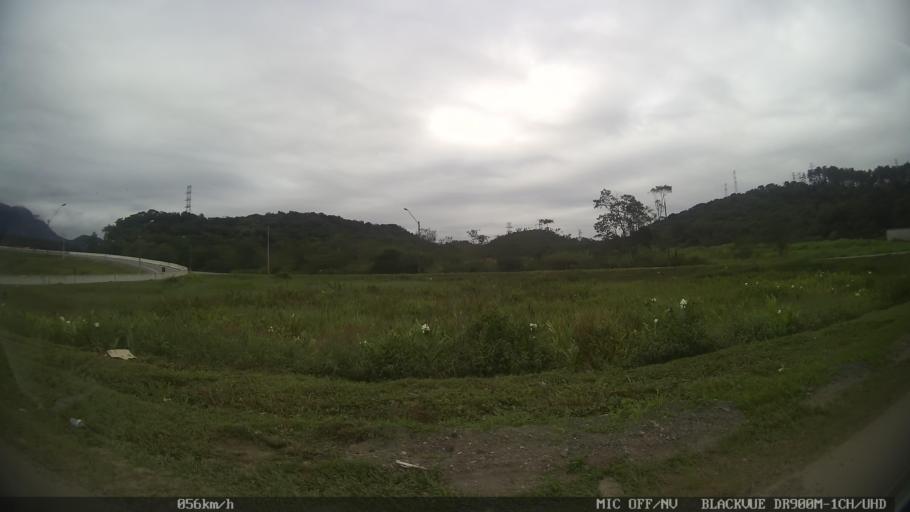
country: BR
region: Santa Catarina
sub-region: Joinville
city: Joinville
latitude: -26.2567
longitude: -48.9035
